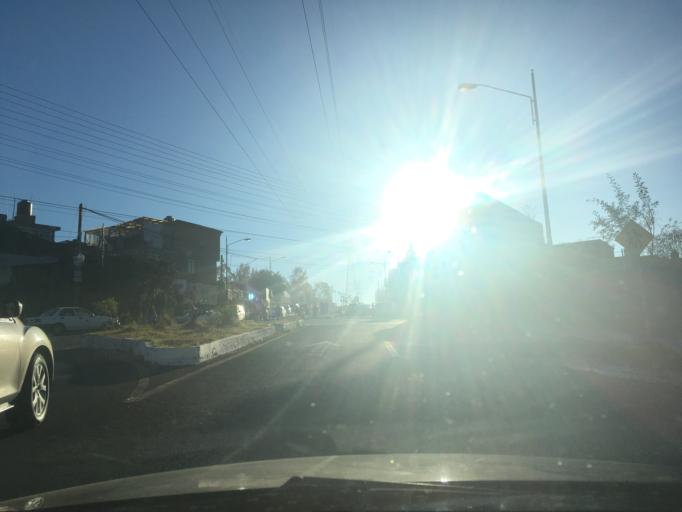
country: MX
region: Michoacan
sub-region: Morelia
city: Montana Monarca (Punta Altozano)
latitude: 19.6578
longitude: -101.1961
